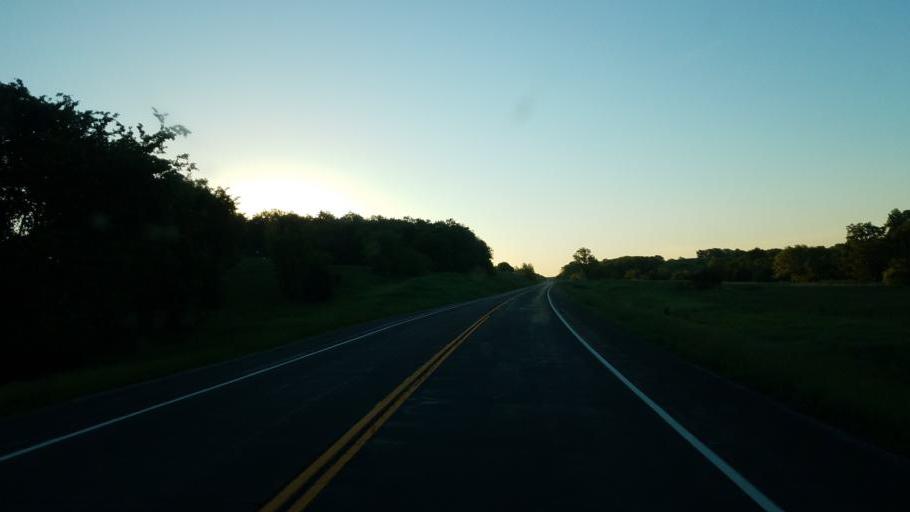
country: US
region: Missouri
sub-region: Schuyler County
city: Lancaster
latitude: 40.4921
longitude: -92.6034
